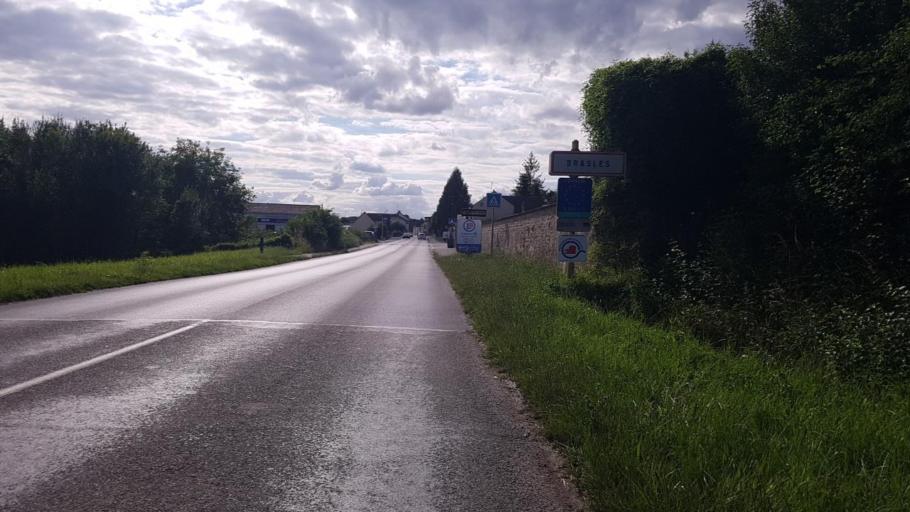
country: FR
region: Picardie
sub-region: Departement de l'Aisne
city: Brasles
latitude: 49.0471
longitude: 3.4342
